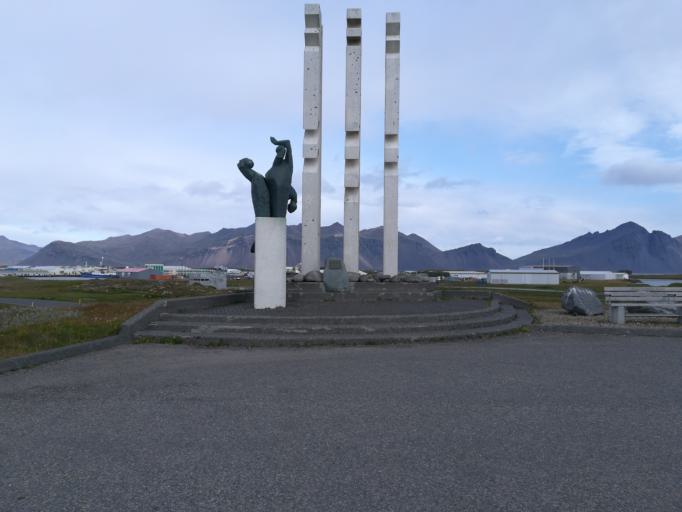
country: IS
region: East
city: Hoefn
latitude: 64.2442
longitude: -15.2051
